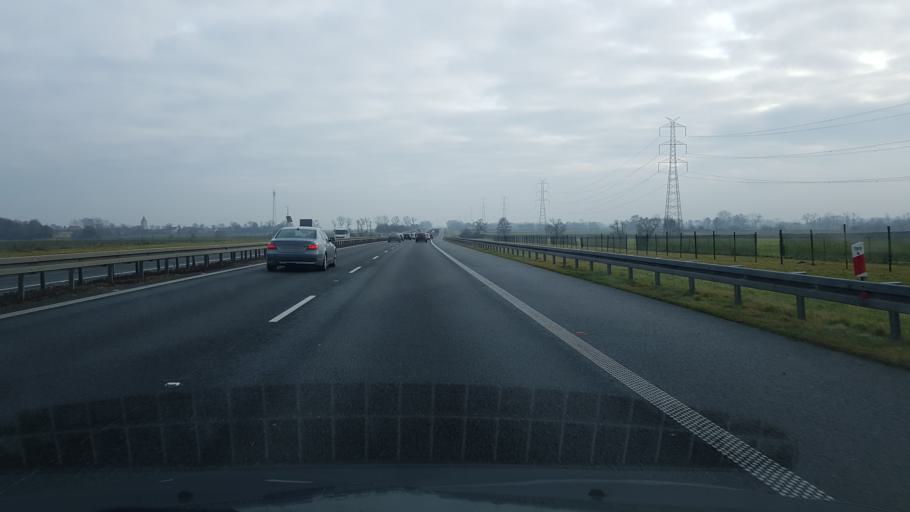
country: PL
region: Lower Silesian Voivodeship
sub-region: Powiat strzelinski
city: Wiazow
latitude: 50.8149
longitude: 17.3092
